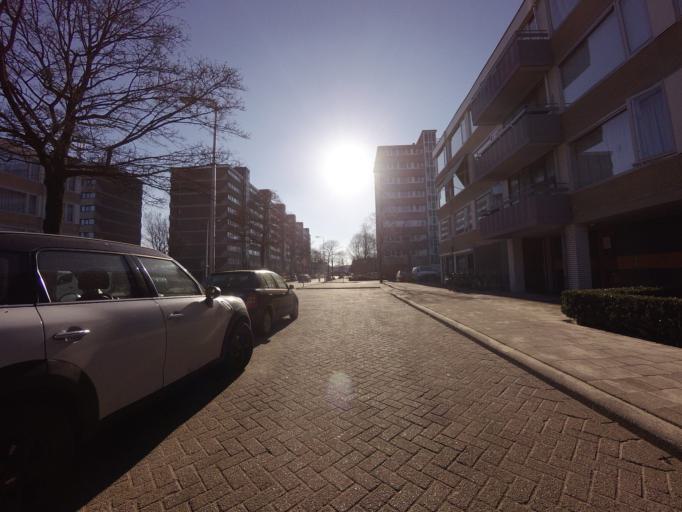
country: NL
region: Utrecht
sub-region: Gemeente Utrecht
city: Utrecht
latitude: 52.1163
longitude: 5.1137
